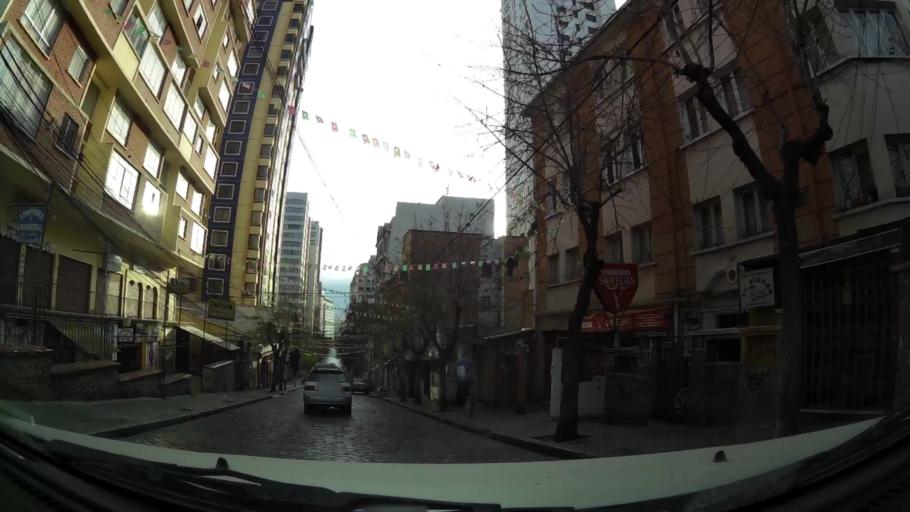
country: BO
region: La Paz
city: La Paz
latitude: -16.5095
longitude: -68.1299
